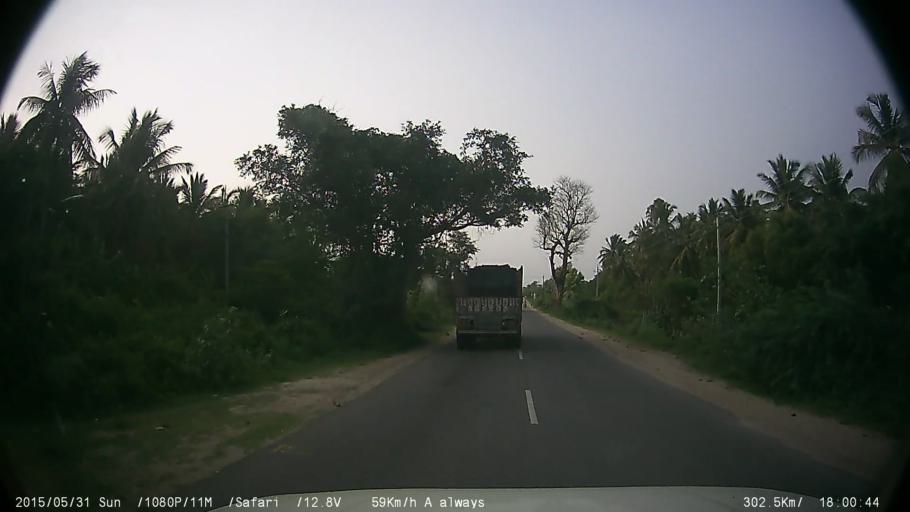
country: IN
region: Karnataka
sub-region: Mysore
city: Nanjangud
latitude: 12.0235
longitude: 76.6732
